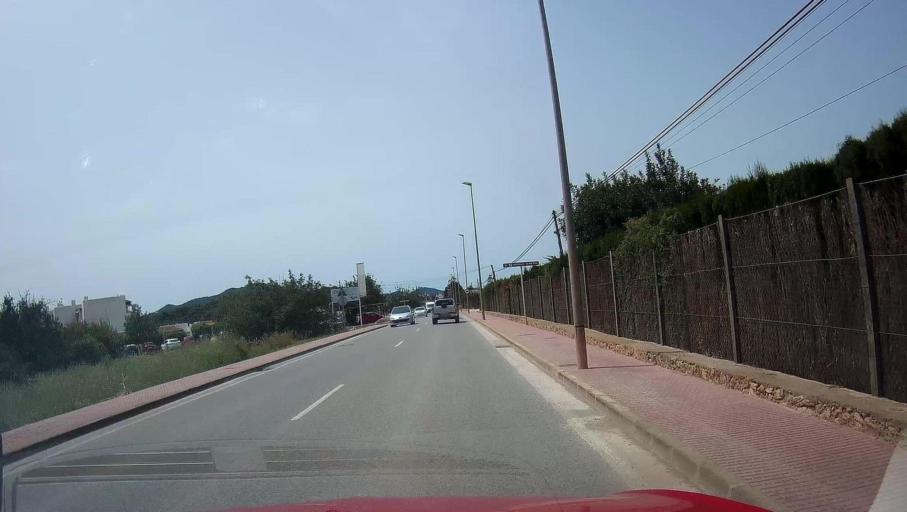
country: ES
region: Balearic Islands
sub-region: Illes Balears
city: Santa Eularia des Riu
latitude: 38.9940
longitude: 1.5511
